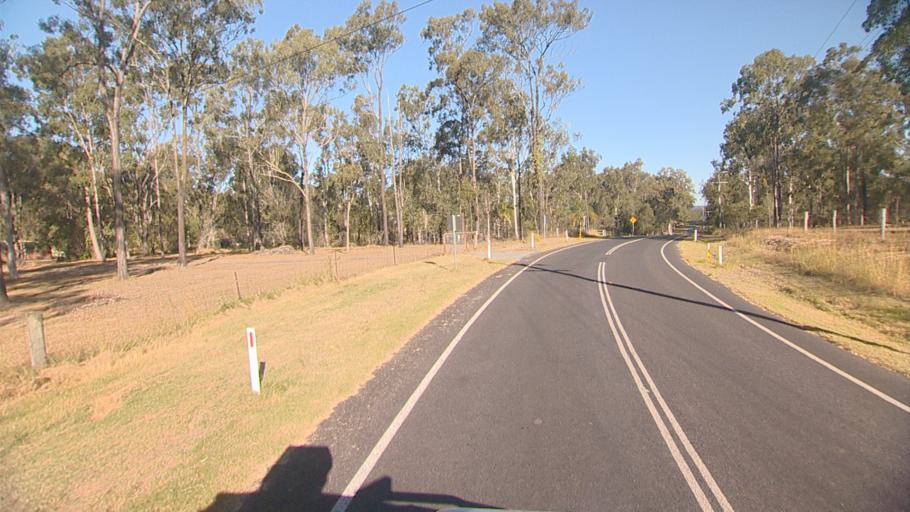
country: AU
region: Queensland
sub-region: Logan
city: North Maclean
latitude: -27.8046
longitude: 153.0341
